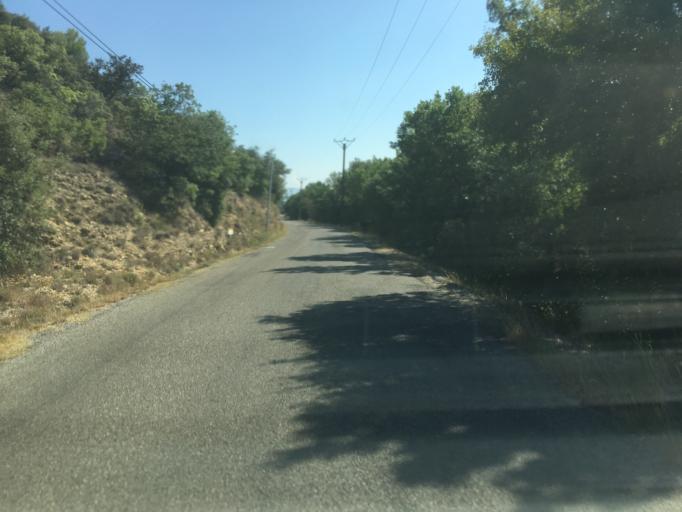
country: FR
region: Provence-Alpes-Cote d'Azur
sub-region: Departement des Alpes-de-Haute-Provence
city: Valensole
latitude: 43.8988
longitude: 6.0169
